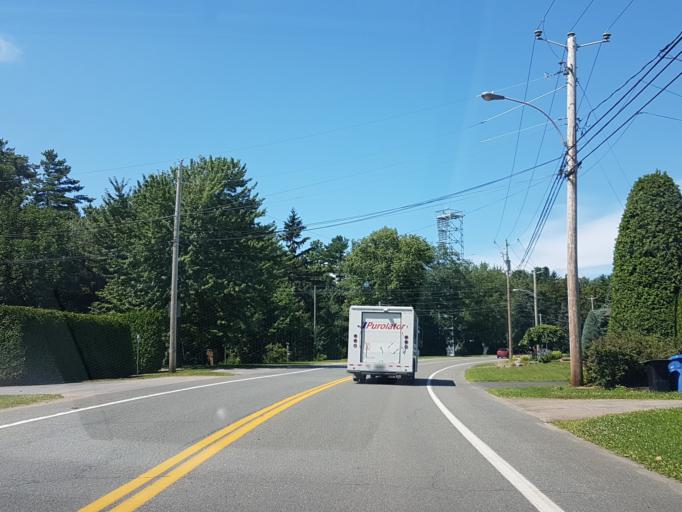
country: CA
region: Quebec
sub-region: Mauricie
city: Nicolet
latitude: 46.2791
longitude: -72.6687
